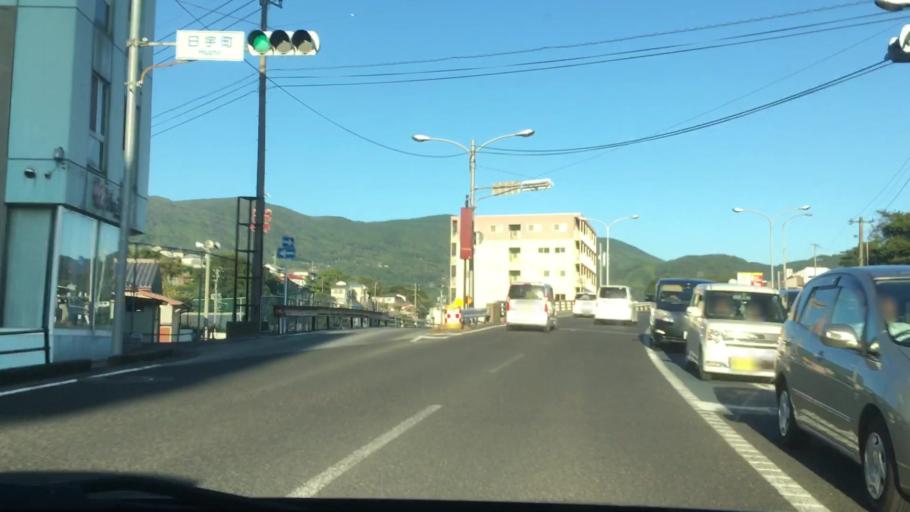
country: JP
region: Nagasaki
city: Sasebo
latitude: 33.1587
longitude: 129.7594
